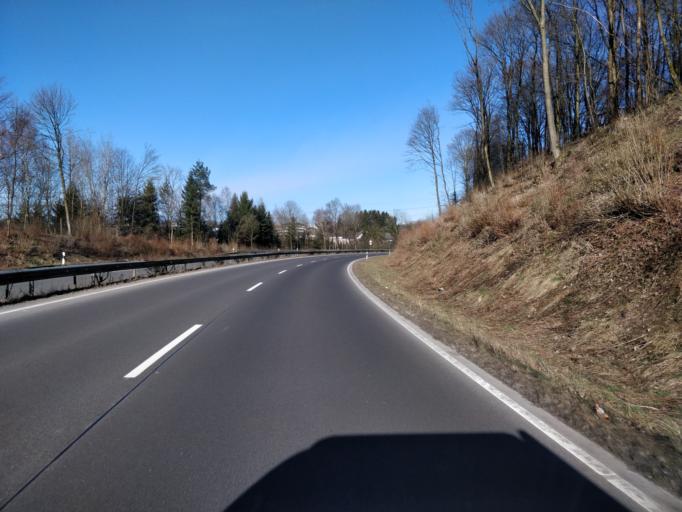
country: DE
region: North Rhine-Westphalia
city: Wiehl
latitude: 50.9671
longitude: 7.5157
